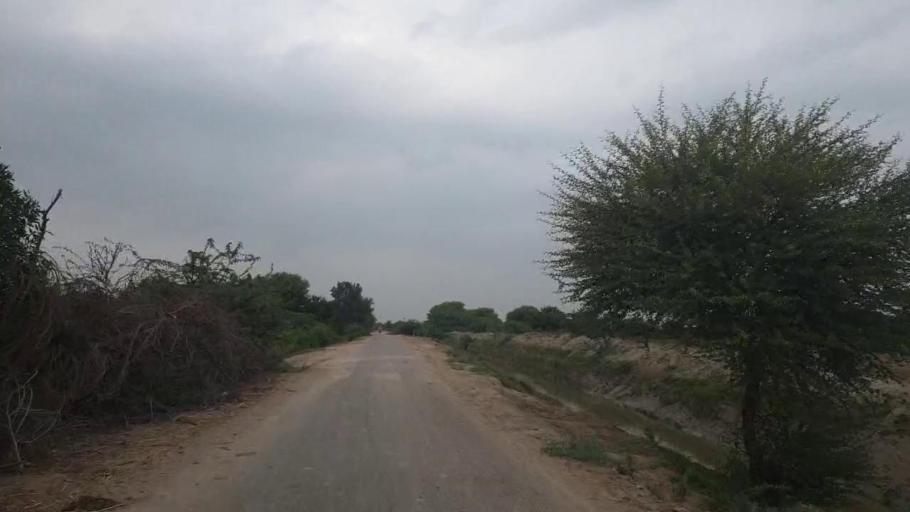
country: PK
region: Sindh
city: Badin
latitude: 24.6235
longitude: 68.6823
